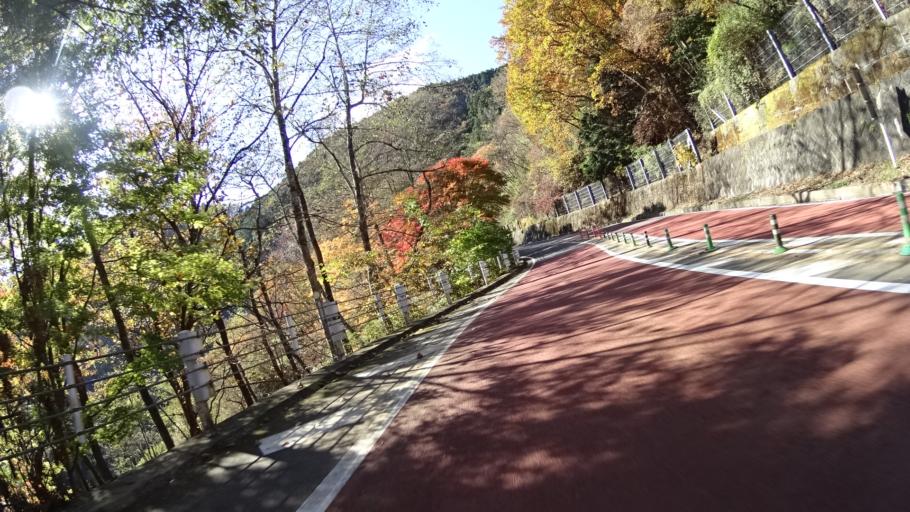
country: JP
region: Yamanashi
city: Uenohara
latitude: 35.7426
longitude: 139.0437
